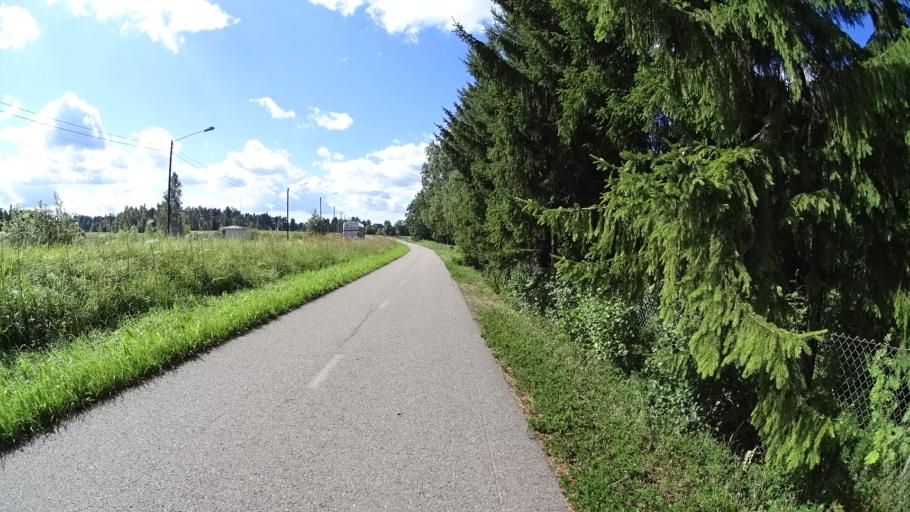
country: FI
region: Uusimaa
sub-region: Helsinki
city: Jaervenpaeae
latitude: 60.4514
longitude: 25.0796
